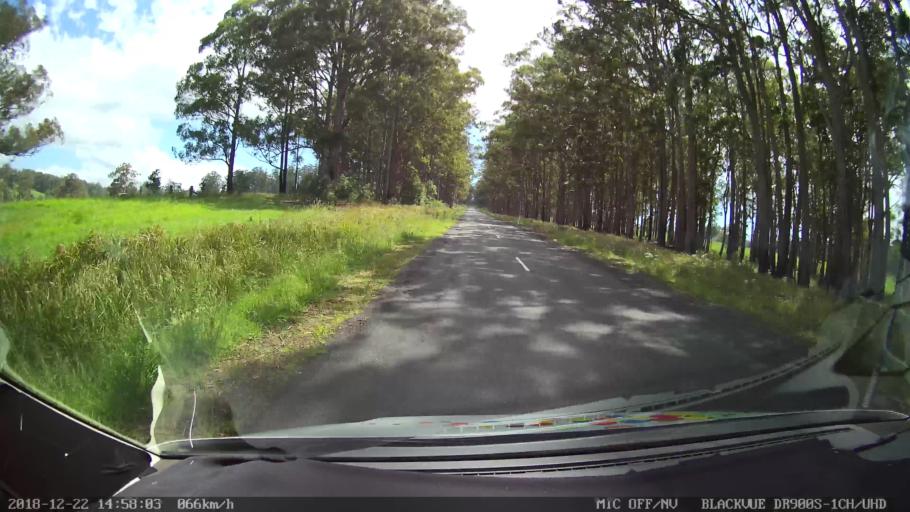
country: AU
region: New South Wales
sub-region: Bellingen
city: Dorrigo
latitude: -30.2379
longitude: 152.4948
